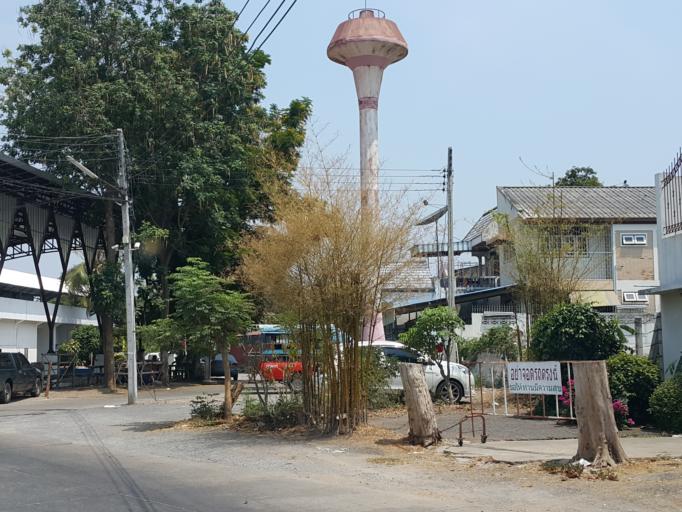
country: TH
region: Kanchanaburi
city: Kanchanaburi
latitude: 14.0229
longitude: 99.5278
